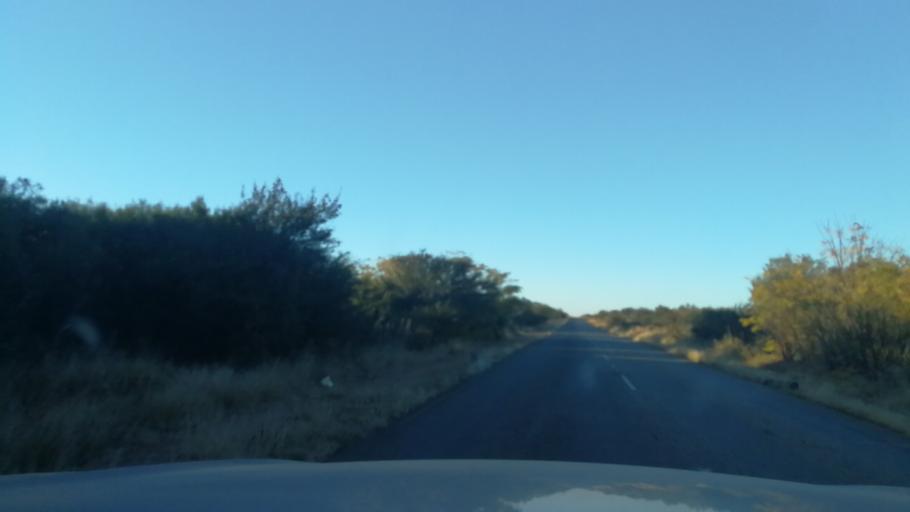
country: ZA
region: North-West
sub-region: Bojanala Platinum District Municipality
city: Koster
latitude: -25.6807
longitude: 26.7270
